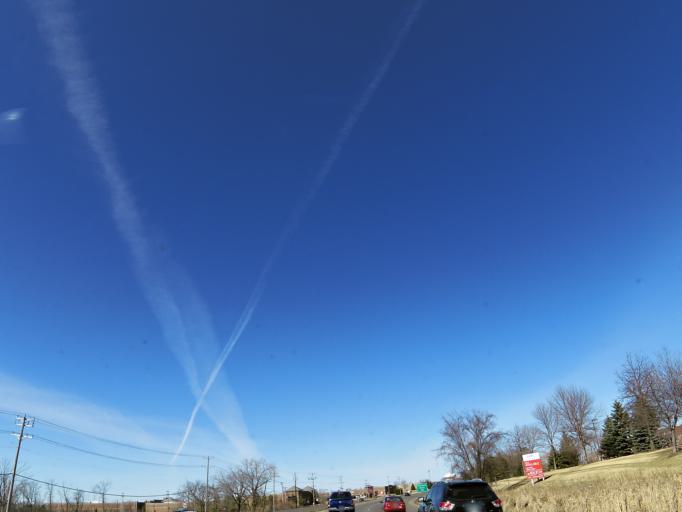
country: US
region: Minnesota
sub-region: Hennepin County
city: Plymouth
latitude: 45.0194
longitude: -93.4875
